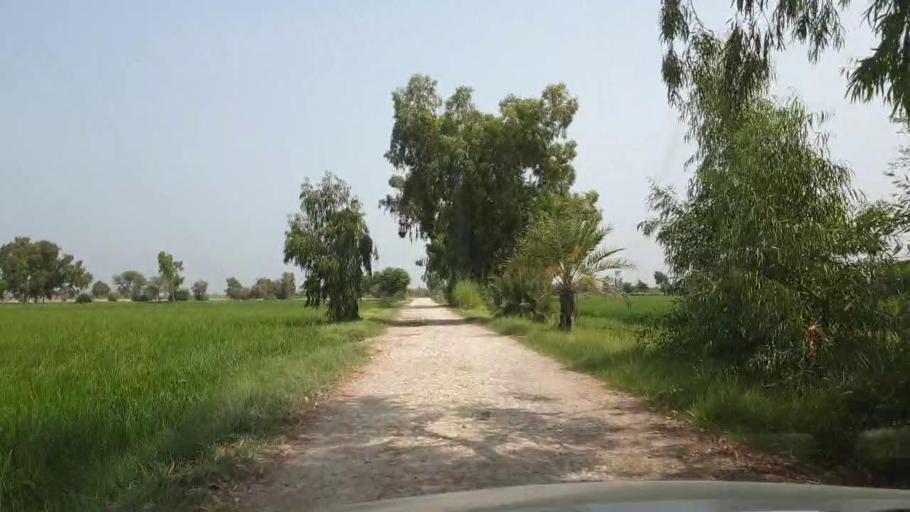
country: PK
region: Sindh
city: Madeji
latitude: 27.7958
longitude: 68.5316
